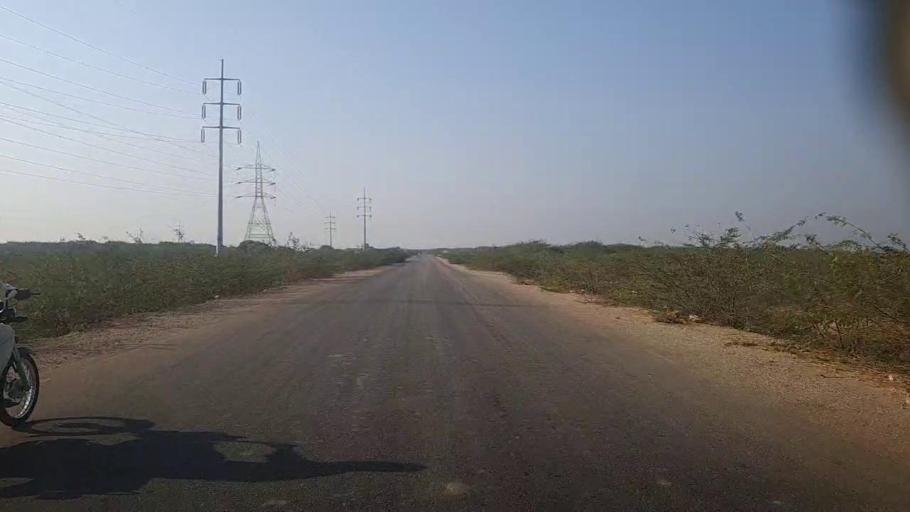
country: PK
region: Sindh
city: Gharo
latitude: 24.7516
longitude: 67.5374
